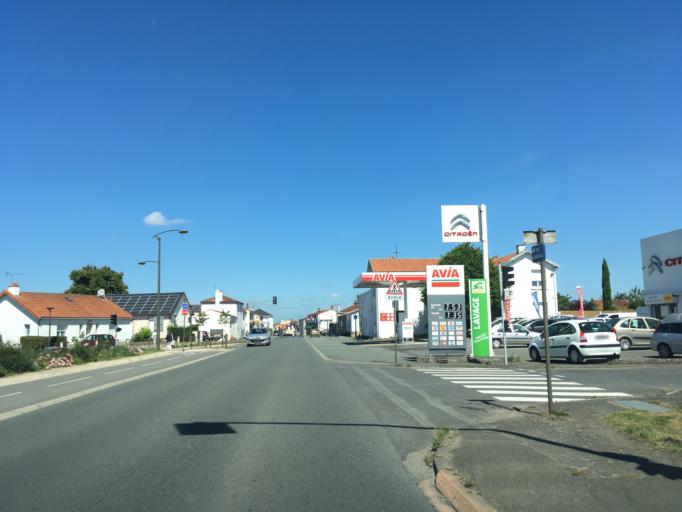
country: FR
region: Pays de la Loire
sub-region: Departement de la Vendee
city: Saint-Georges-de-Montaigu
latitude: 46.9448
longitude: -1.2902
